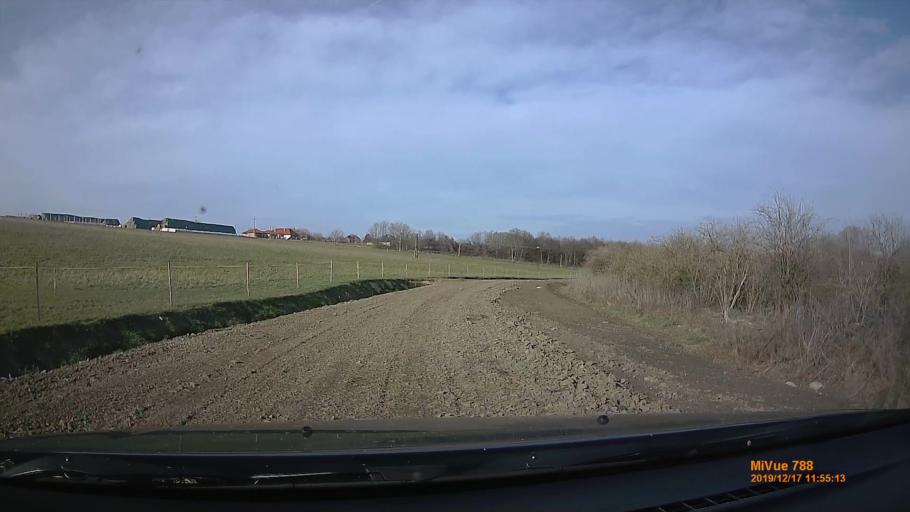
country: HU
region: Somogy
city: Kaposvar
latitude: 46.4527
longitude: 17.7695
